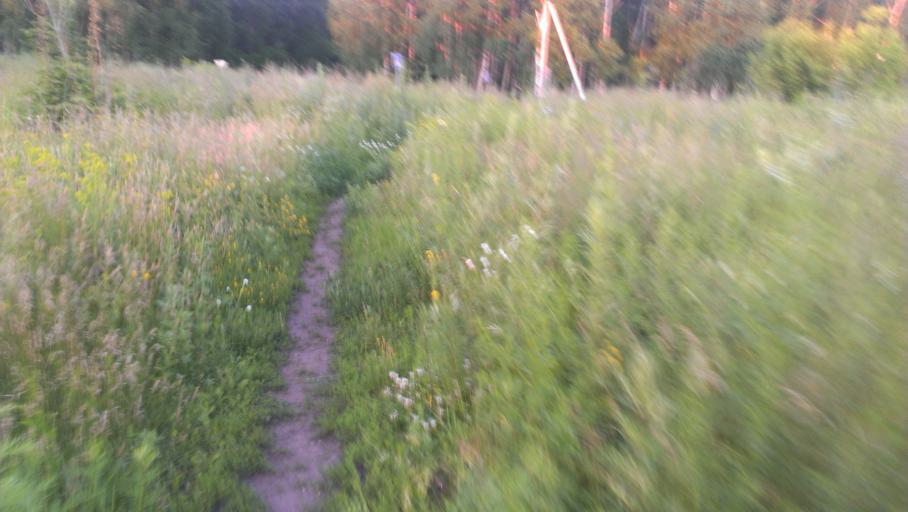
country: RU
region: Altai Krai
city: Novosilikatnyy
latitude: 53.3635
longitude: 83.6561
